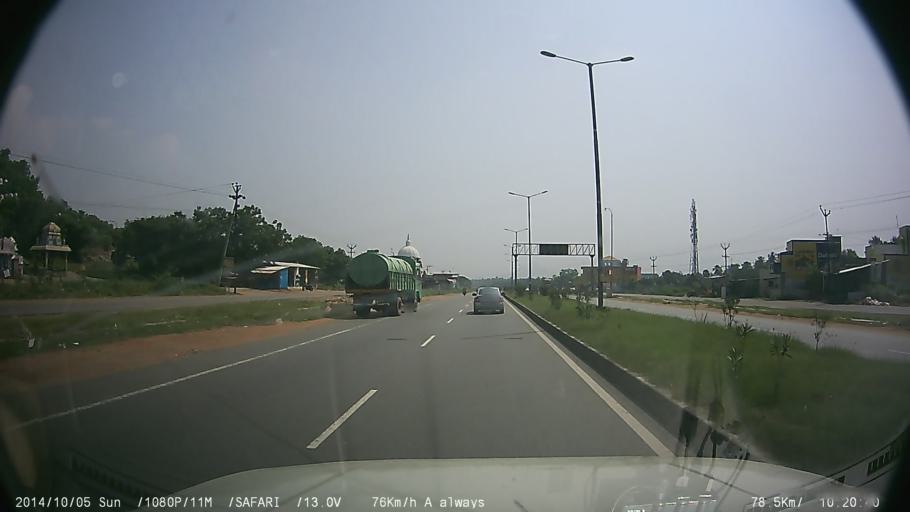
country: IN
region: Tamil Nadu
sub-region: Salem
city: Attayyampatti
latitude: 11.5951
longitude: 78.0804
